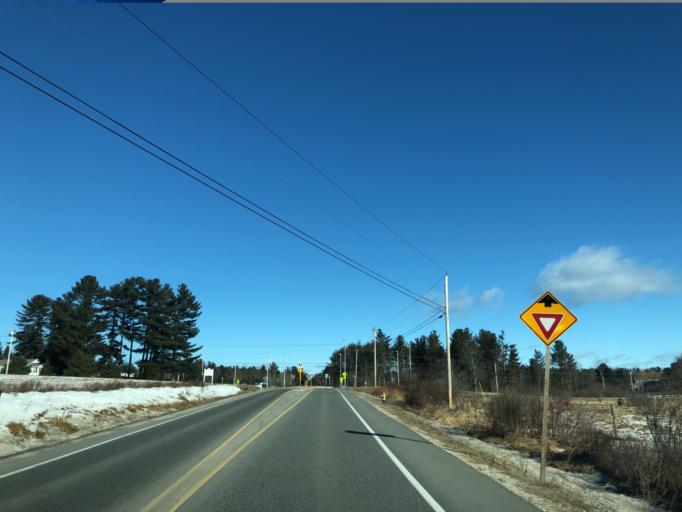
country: US
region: Maine
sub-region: Cumberland County
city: North Windham
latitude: 43.7977
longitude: -70.4401
